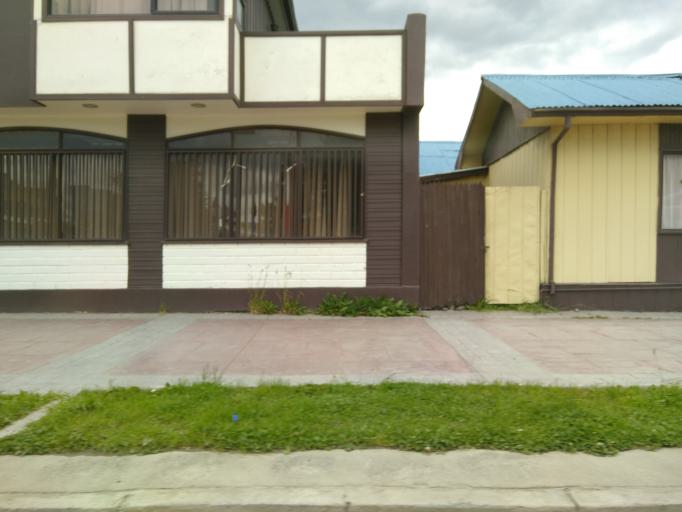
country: CL
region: Magallanes
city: Puerto Natales
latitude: -51.7291
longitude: -72.5024
